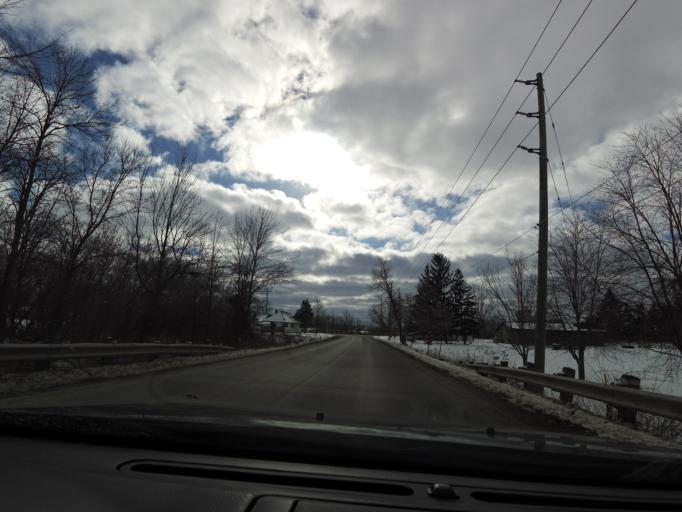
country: CA
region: Ontario
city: Hamilton
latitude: 43.1178
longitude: -79.6572
